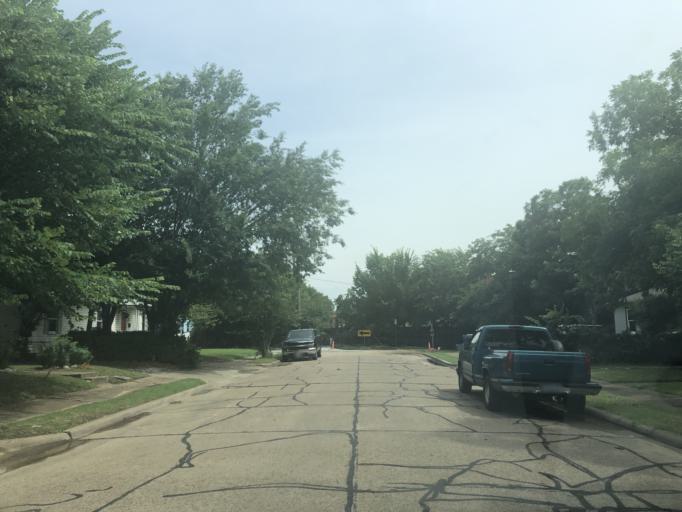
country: US
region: Texas
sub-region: Dallas County
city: Irving
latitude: 32.8118
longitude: -96.9724
